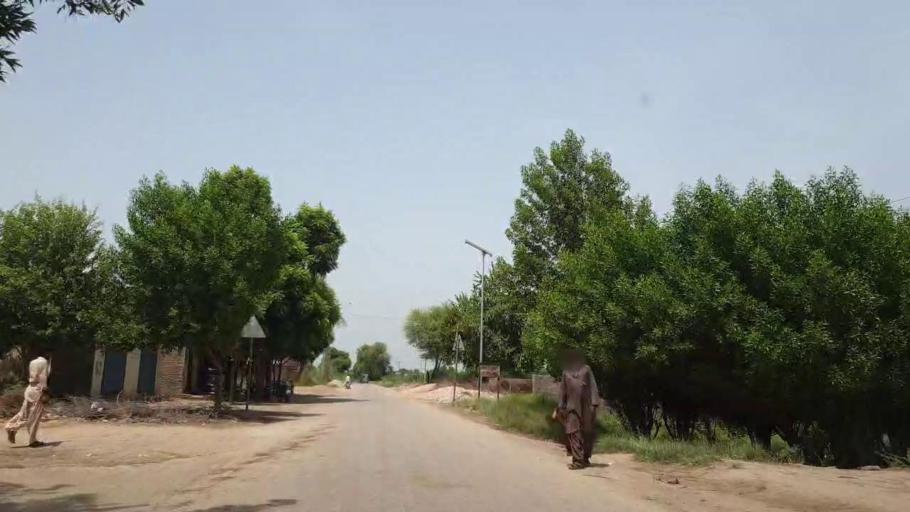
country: PK
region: Sindh
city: Sakrand
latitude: 26.1989
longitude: 68.2408
